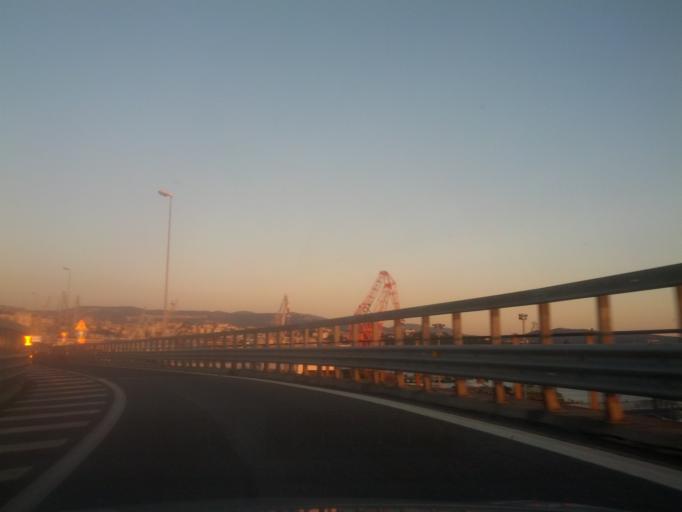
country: IT
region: Friuli Venezia Giulia
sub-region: Provincia di Trieste
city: Trieste
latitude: 45.6379
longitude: 13.7646
